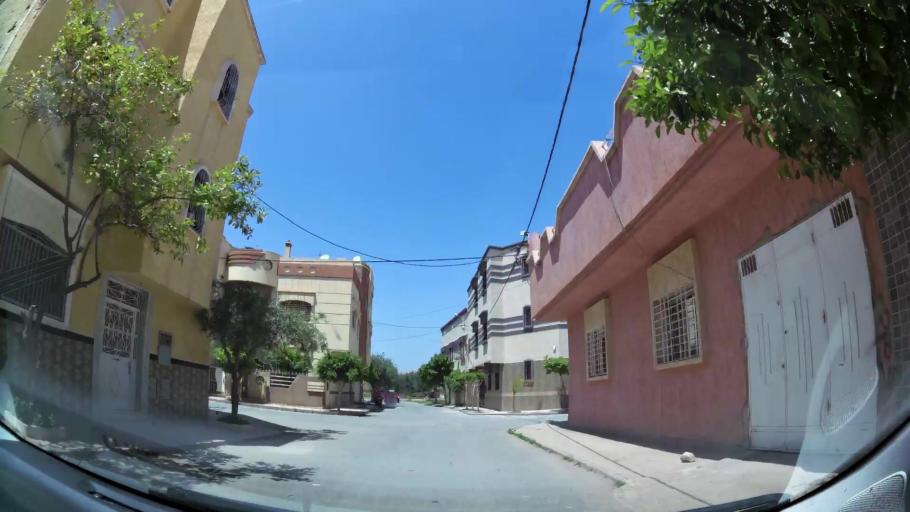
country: MA
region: Oriental
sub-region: Oujda-Angad
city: Oujda
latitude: 34.6947
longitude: -1.8977
